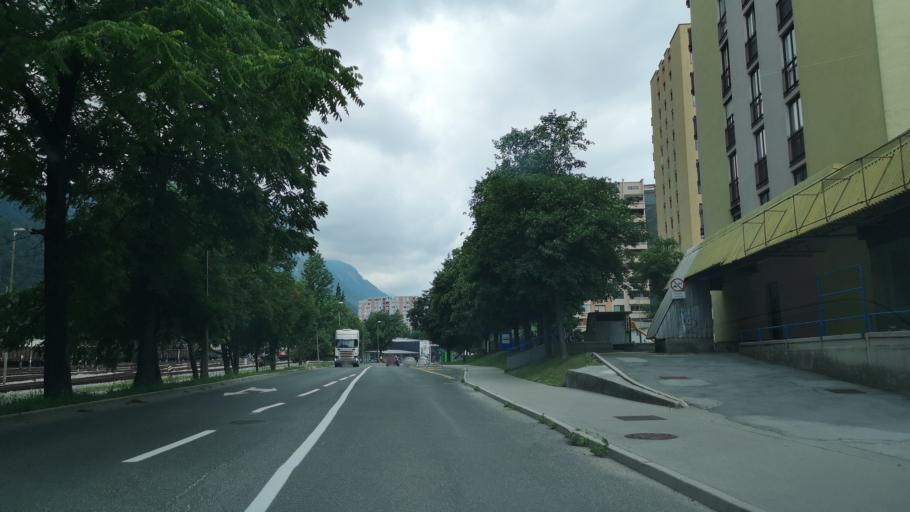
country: SI
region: Jesenice
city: Jesenice
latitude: 46.4370
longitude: 14.0505
